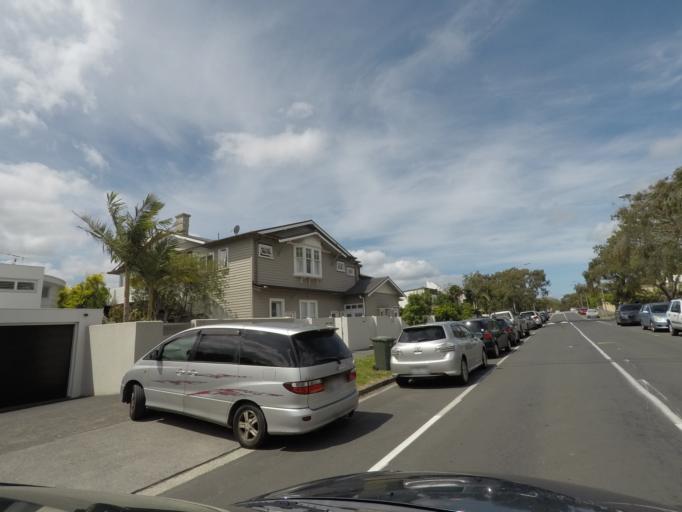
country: NZ
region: Auckland
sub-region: Auckland
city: Auckland
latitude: -36.8416
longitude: 174.7357
